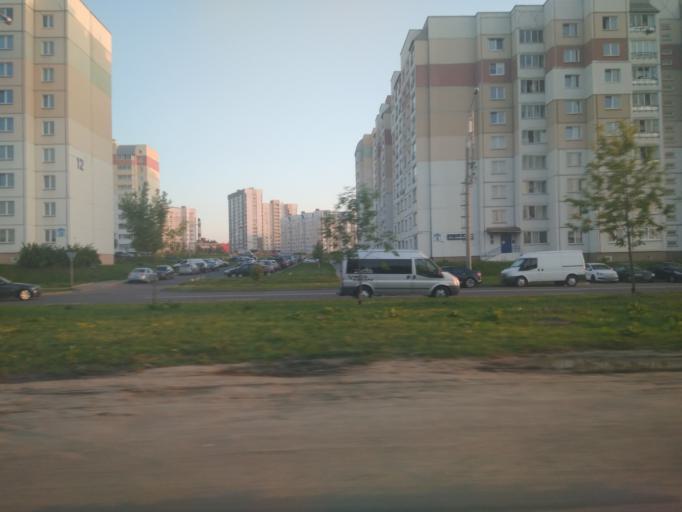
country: BY
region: Minsk
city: Novoye Medvezhino
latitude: 53.9213
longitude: 27.4615
